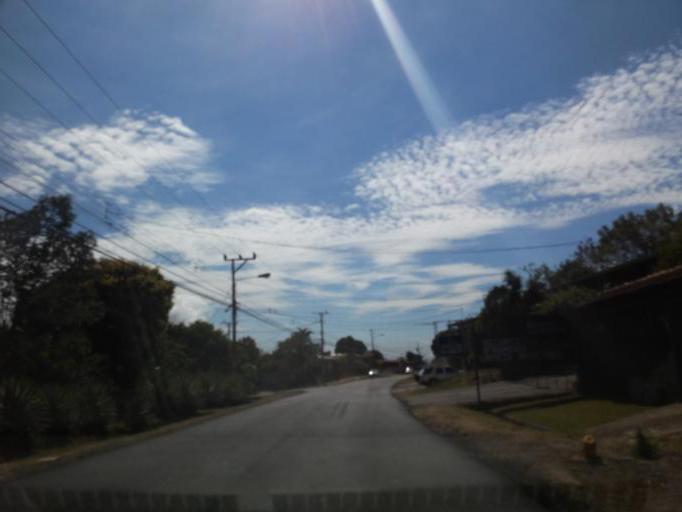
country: CR
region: Heredia
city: Santo Domingo
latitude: 10.0318
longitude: -84.1668
